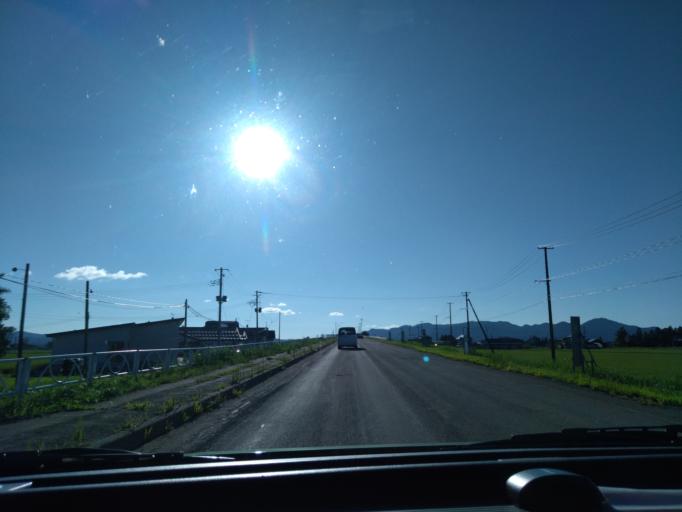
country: JP
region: Akita
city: Omagari
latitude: 39.4227
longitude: 140.5093
